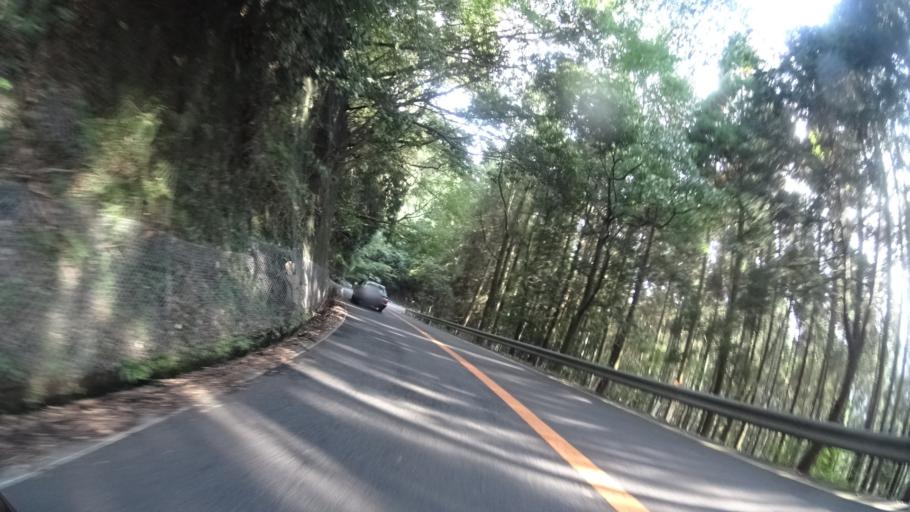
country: JP
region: Oita
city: Beppu
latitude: 33.2655
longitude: 131.3710
